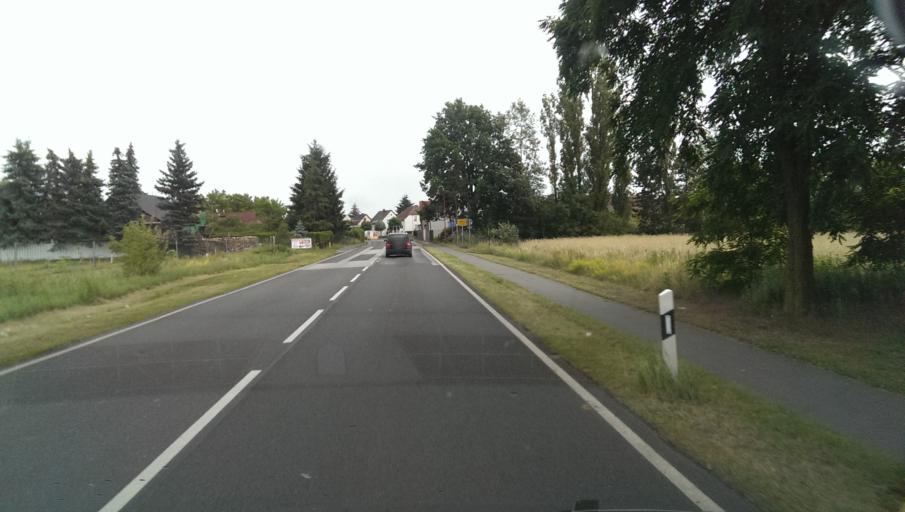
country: DE
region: Brandenburg
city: Premnitz
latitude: 52.5228
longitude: 12.3632
